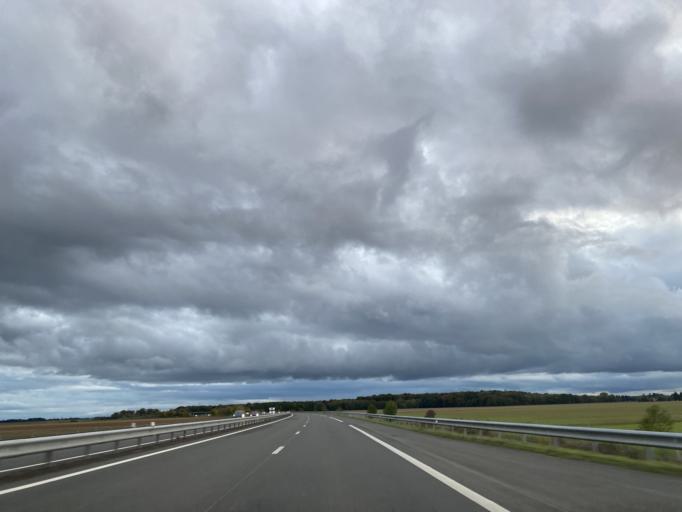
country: FR
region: Centre
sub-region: Departement du Cher
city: Levet
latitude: 46.9477
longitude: 2.4163
